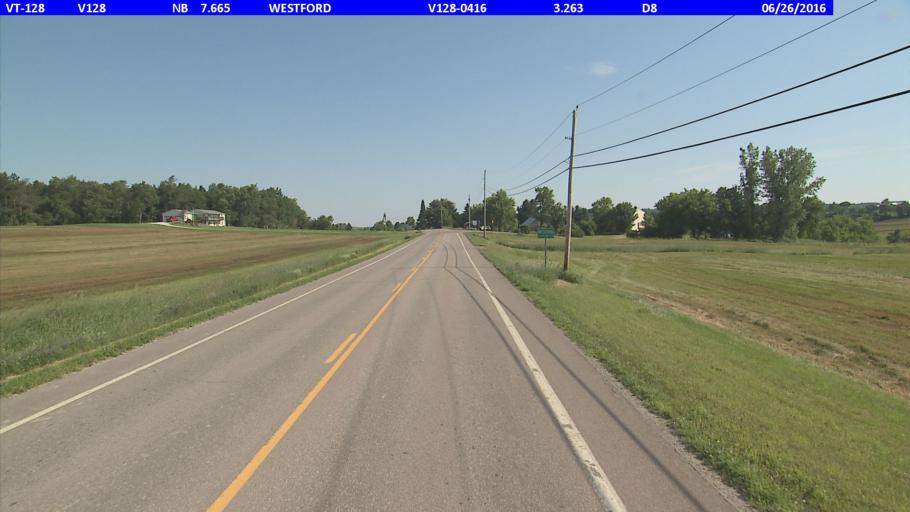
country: US
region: Vermont
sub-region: Chittenden County
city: Jericho
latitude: 44.6040
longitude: -73.0089
